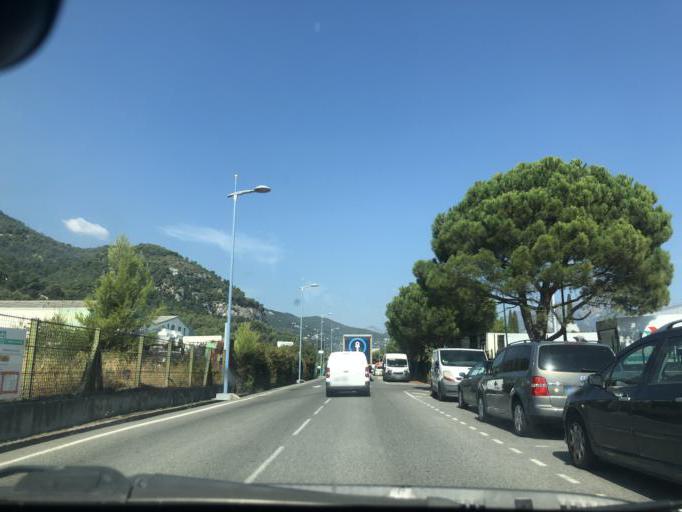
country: FR
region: Provence-Alpes-Cote d'Azur
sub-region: Departement des Alpes-Maritimes
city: Carros
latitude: 43.7935
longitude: 7.2023
